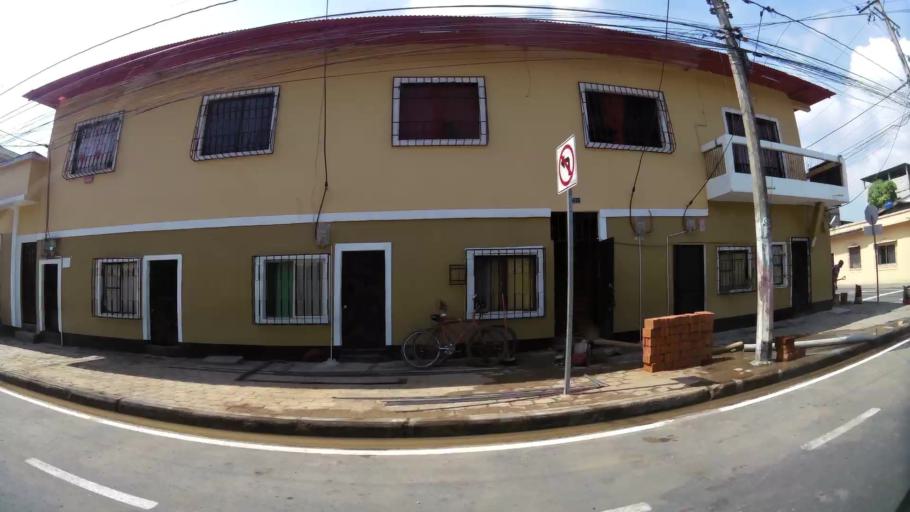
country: EC
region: Guayas
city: Eloy Alfaro
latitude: -2.1601
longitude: -79.8424
